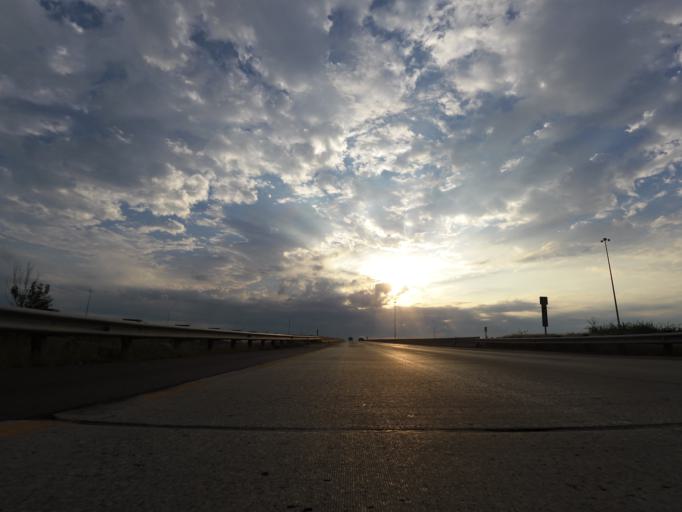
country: US
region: Kansas
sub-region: Sedgwick County
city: Park City
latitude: 37.7550
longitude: -97.3750
